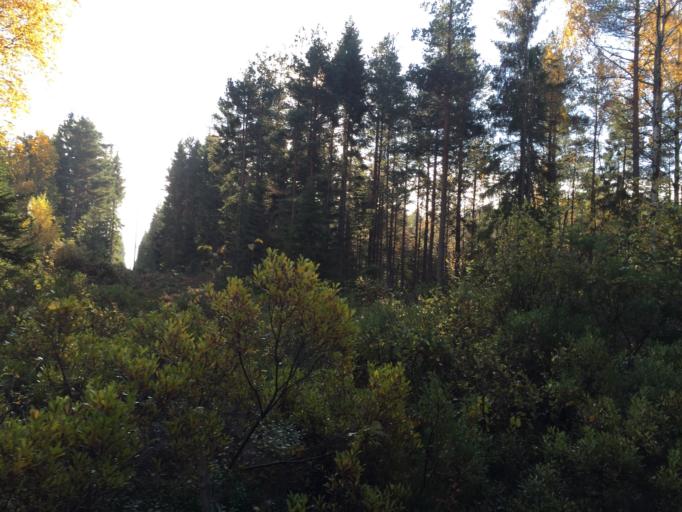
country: SE
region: Vaestra Goetaland
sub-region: Vara Kommun
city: Vara
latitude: 58.3757
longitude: 12.9330
